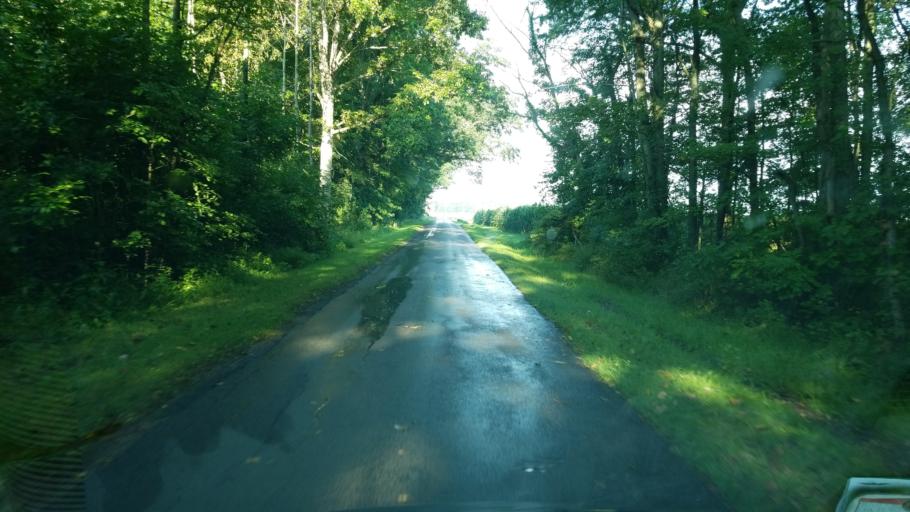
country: US
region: Ohio
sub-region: Crawford County
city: Bucyrus
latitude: 40.7474
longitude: -82.9175
